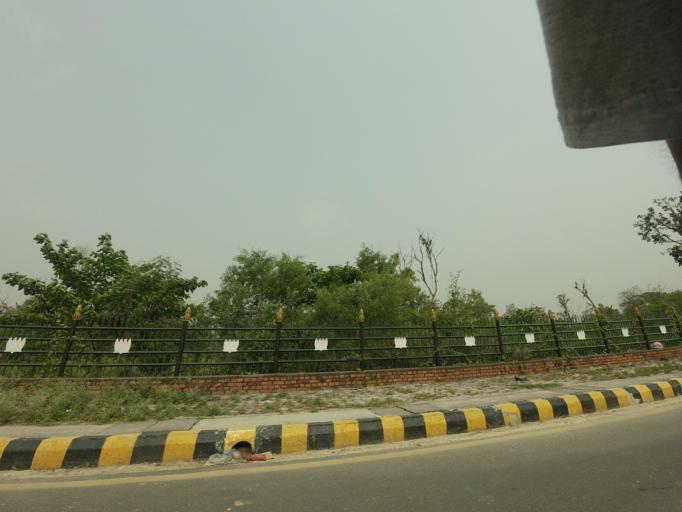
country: IN
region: Uttar Pradesh
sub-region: Maharajganj
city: Nautanwa
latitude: 27.4665
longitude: 83.2837
